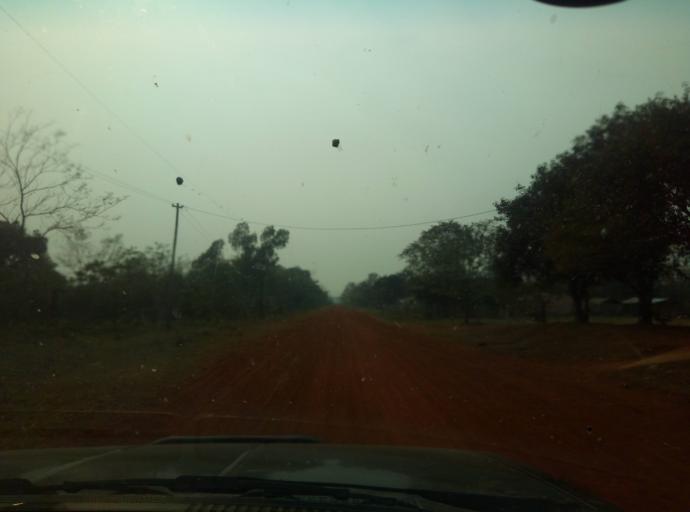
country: PY
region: Caaguazu
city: Carayao
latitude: -25.2042
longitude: -56.2492
